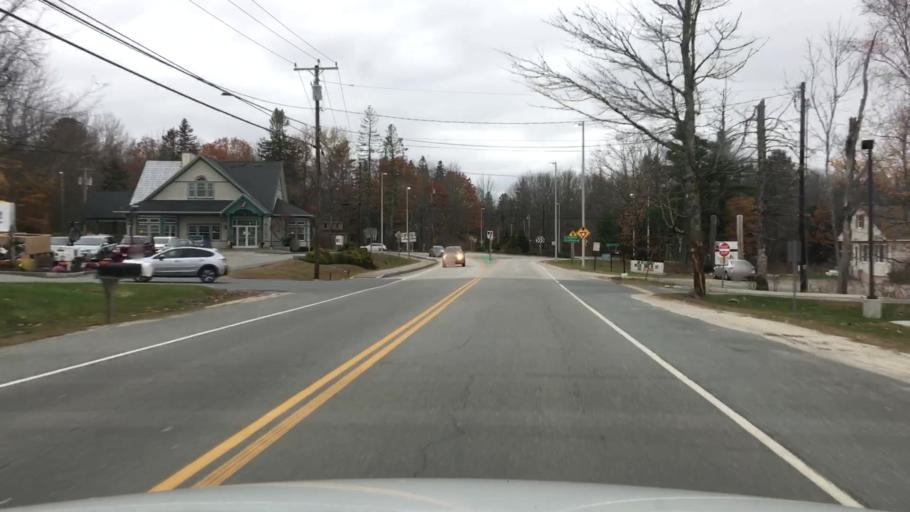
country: US
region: Maine
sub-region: Hancock County
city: Sedgwick
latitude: 44.4072
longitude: -68.5965
